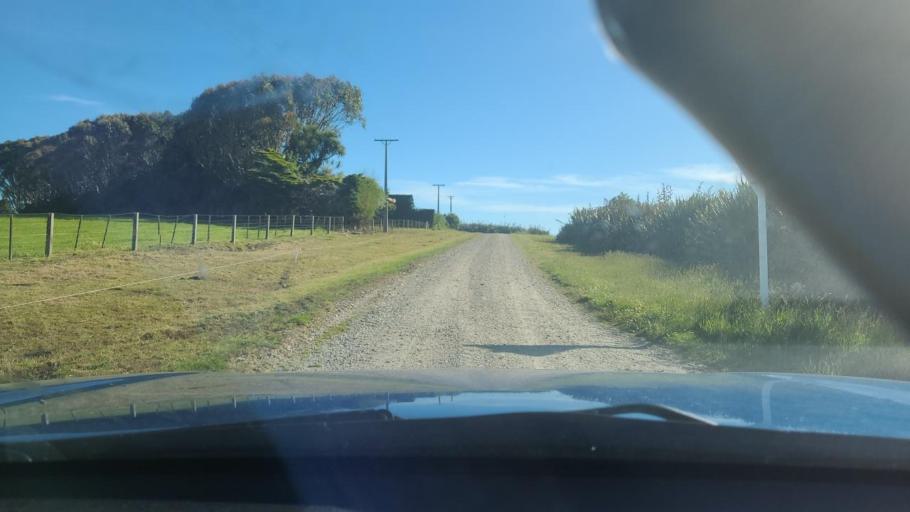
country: NZ
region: Southland
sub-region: Gore District
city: Gore
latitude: -46.2714
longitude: 168.7500
